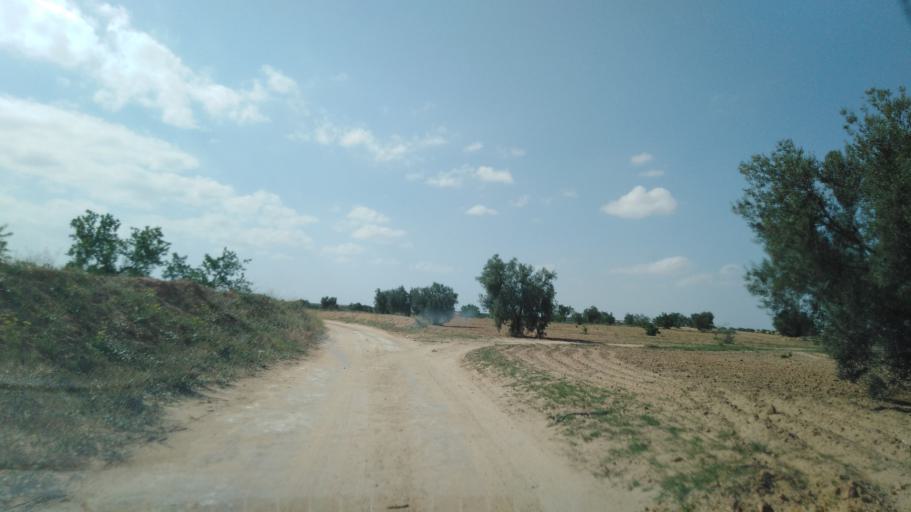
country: TN
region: Safaqis
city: Bi'r `Ali Bin Khalifah
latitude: 34.7965
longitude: 10.3911
